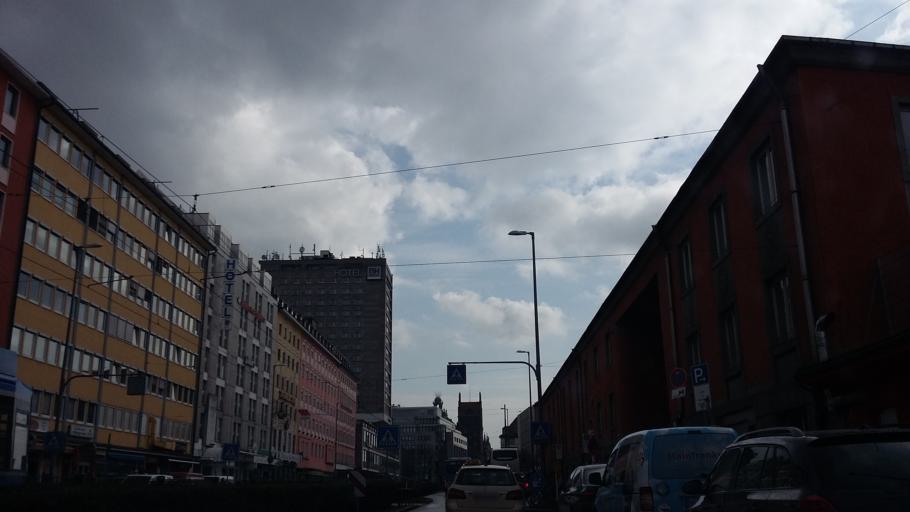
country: DE
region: Bavaria
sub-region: Upper Bavaria
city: Munich
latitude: 48.1419
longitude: 11.5572
